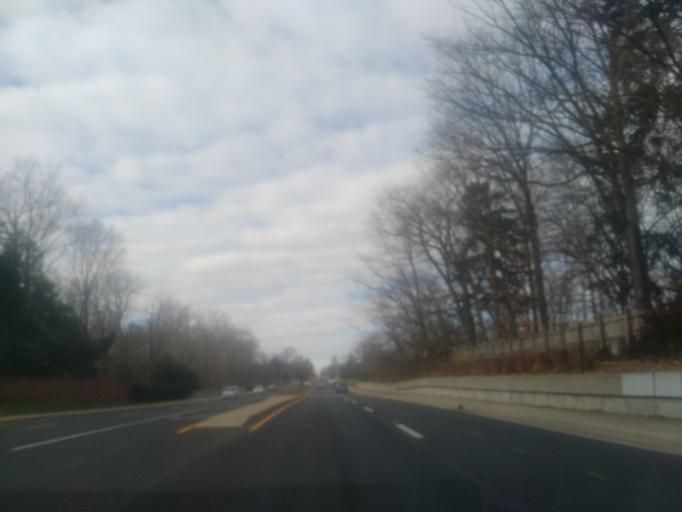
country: US
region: Indiana
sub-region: Marion County
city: Meridian Hills
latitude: 39.9124
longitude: -86.1730
